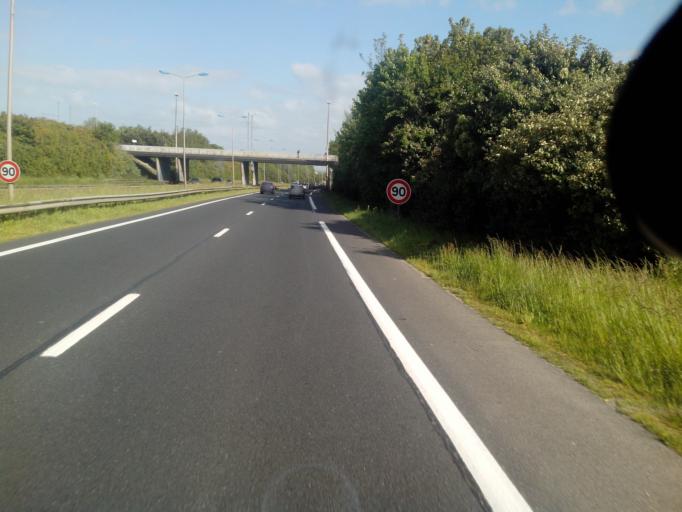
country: FR
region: Lower Normandy
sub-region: Departement du Calvados
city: Caen
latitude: 49.2002
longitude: -0.3465
